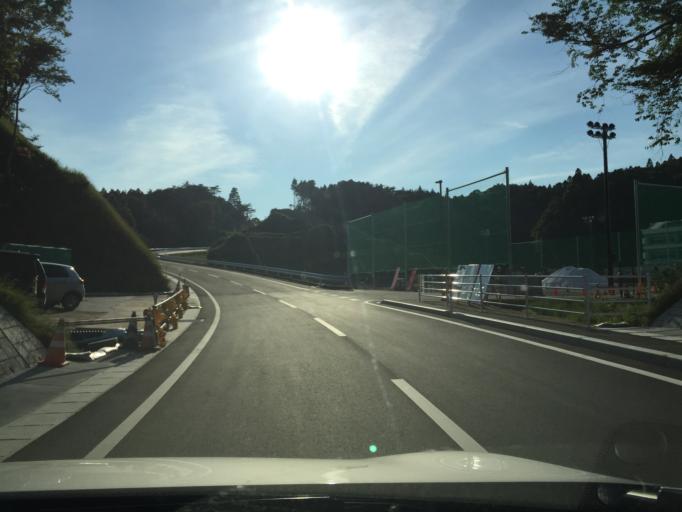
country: JP
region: Fukushima
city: Iwaki
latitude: 37.0001
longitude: 140.9747
